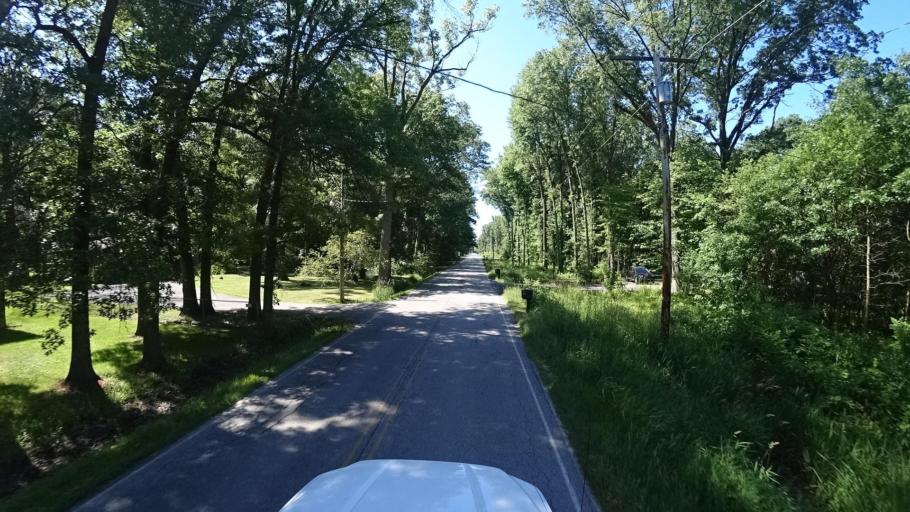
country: US
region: Indiana
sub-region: Porter County
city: Porter
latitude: 41.5989
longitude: -87.1054
